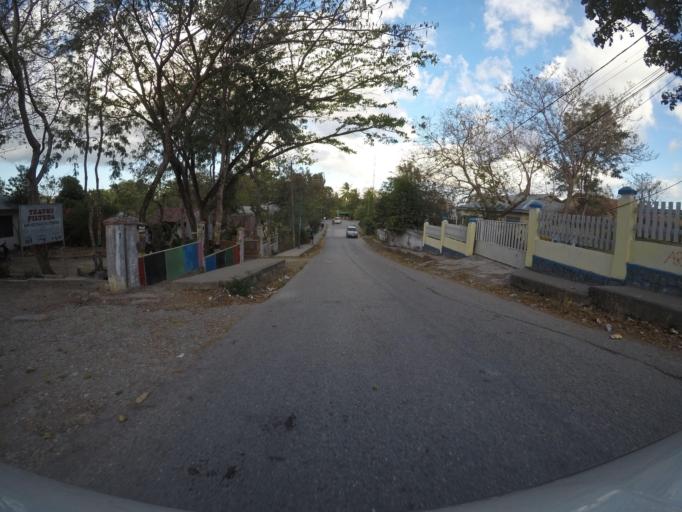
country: TL
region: Baucau
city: Baucau
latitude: -8.4706
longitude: 126.4580
